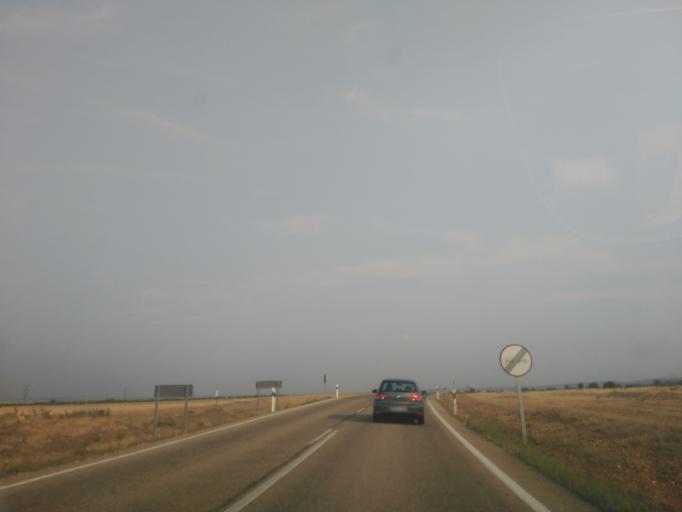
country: ES
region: Castille and Leon
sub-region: Provincia de Zamora
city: Tabara
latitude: 41.8483
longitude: -5.9833
